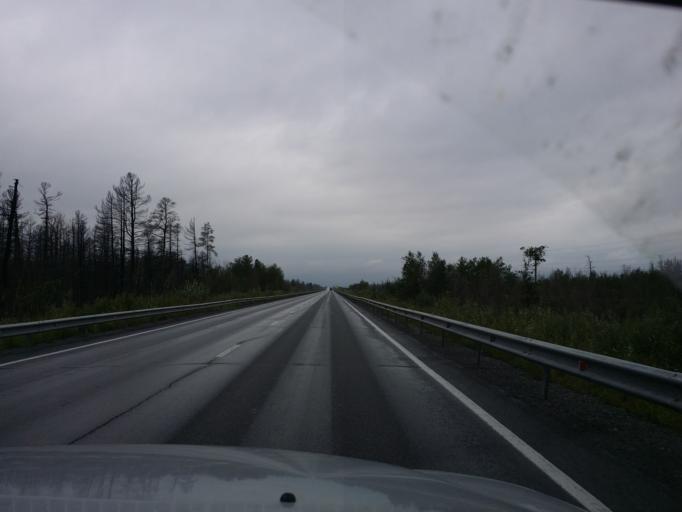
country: RU
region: Khanty-Mansiyskiy Avtonomnyy Okrug
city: Lokosovo
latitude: 61.4533
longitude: 74.6949
